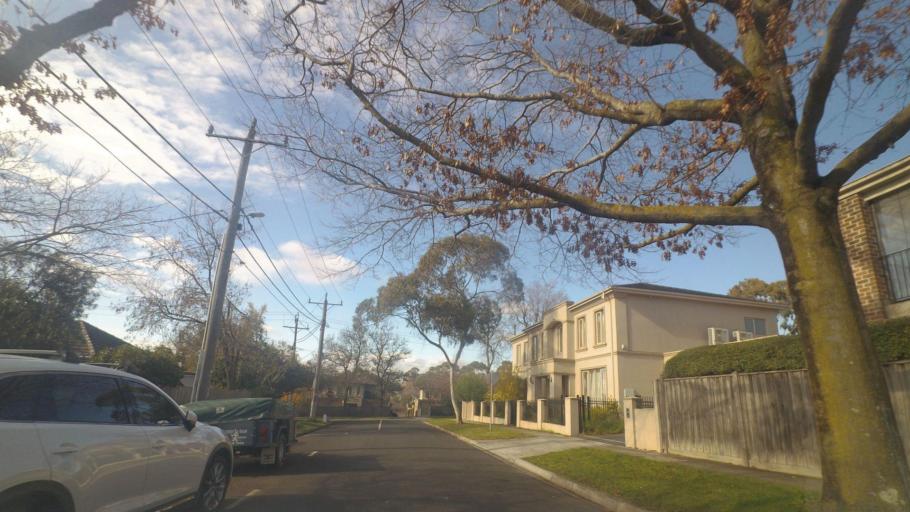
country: AU
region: Victoria
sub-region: Whitehorse
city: Mont Albert North
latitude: -37.8003
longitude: 145.1055
